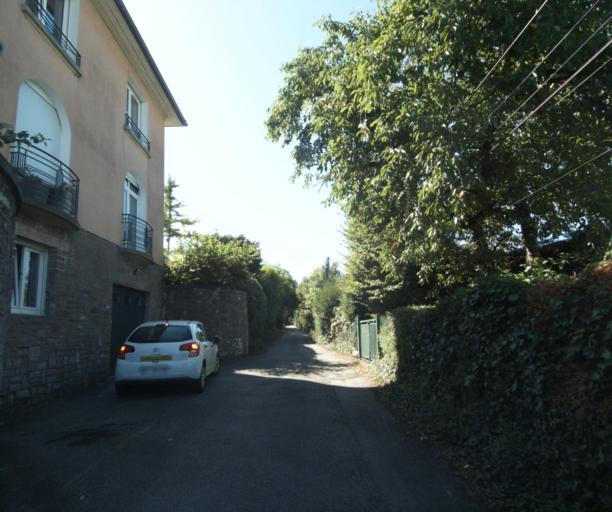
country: FR
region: Lorraine
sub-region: Departement des Vosges
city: Epinal
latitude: 48.1846
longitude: 6.4497
